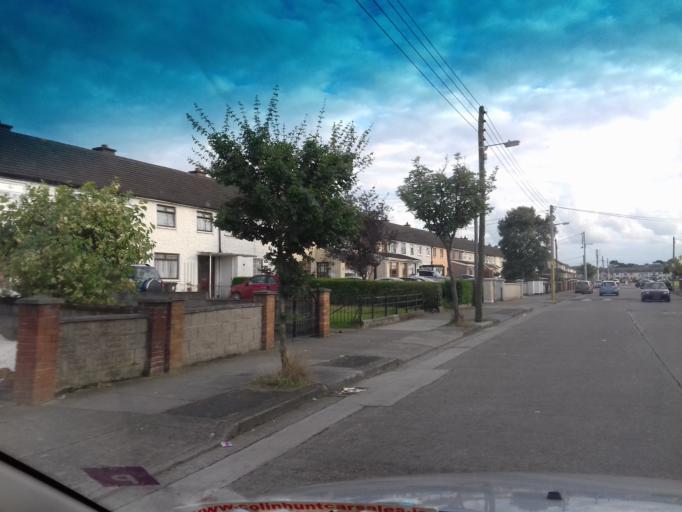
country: IE
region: Leinster
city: Artane
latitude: 53.3961
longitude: -6.2246
